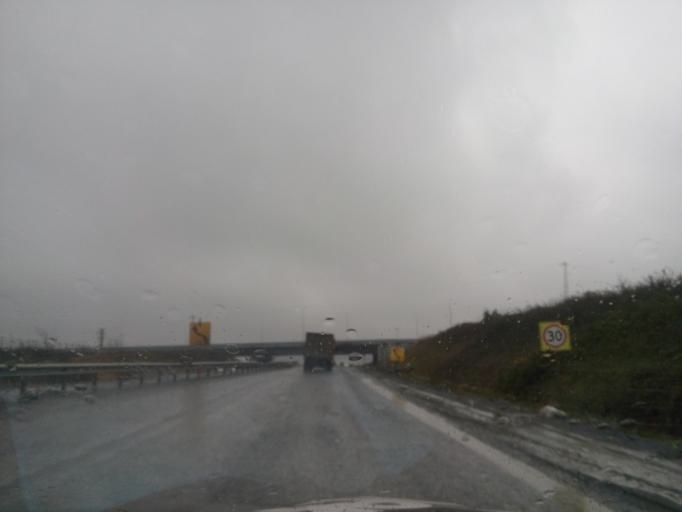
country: TR
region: Istanbul
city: Kemerburgaz
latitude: 41.2356
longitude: 28.8159
